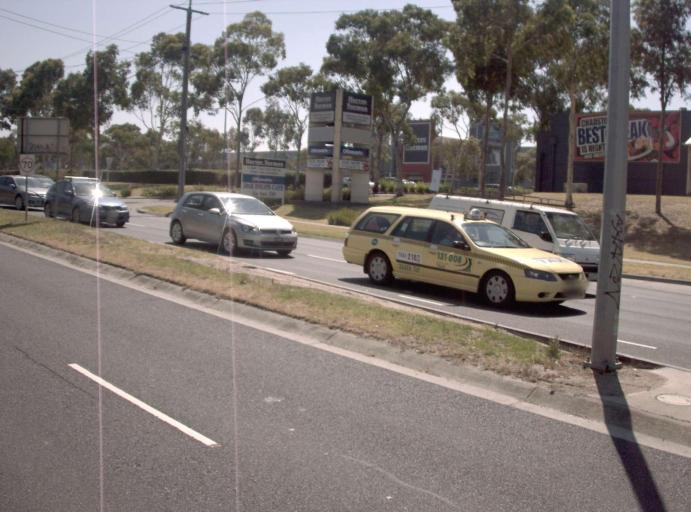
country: AU
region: Victoria
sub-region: Monash
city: Chadstone
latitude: -37.8793
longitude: 145.0908
